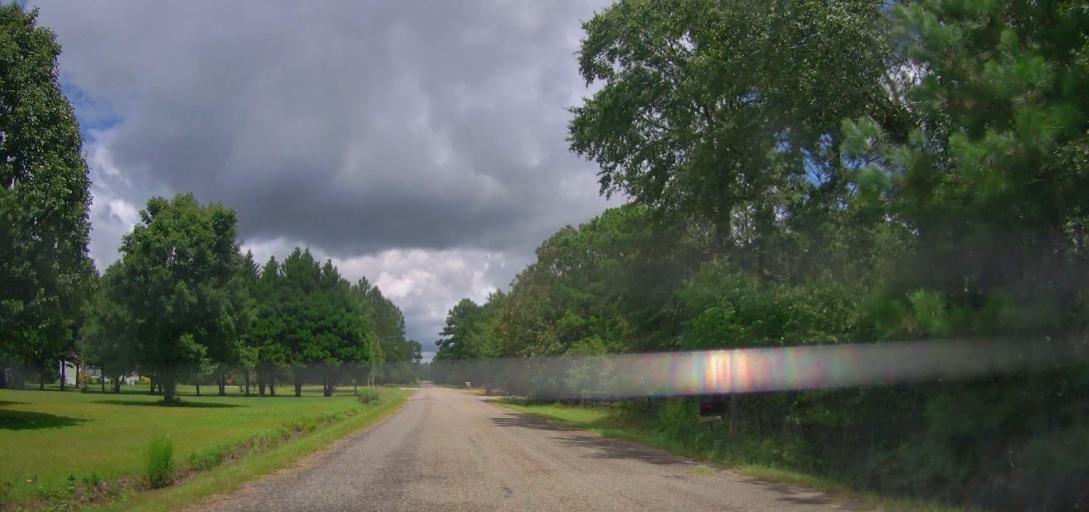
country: US
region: Georgia
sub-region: Pulaski County
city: Hawkinsville
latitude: 32.3277
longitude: -83.5269
